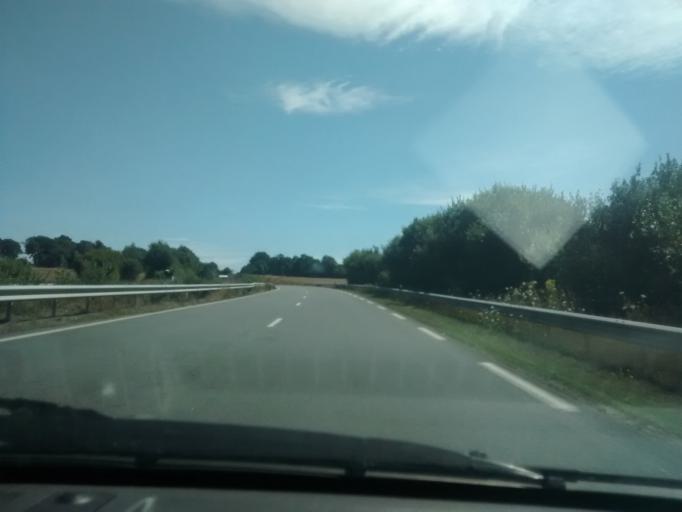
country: FR
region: Brittany
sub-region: Departement des Cotes-d'Armor
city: Begard
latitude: 48.6273
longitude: -3.3206
